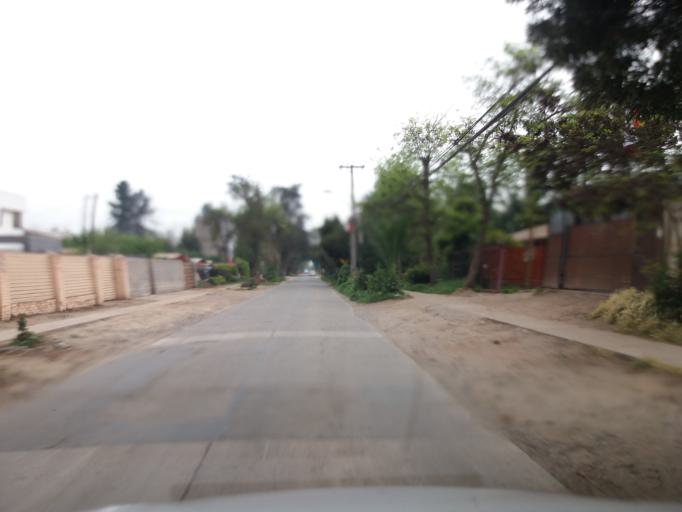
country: CL
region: Valparaiso
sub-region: Provincia de Quillota
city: Hacienda La Calera
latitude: -32.8186
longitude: -71.1347
